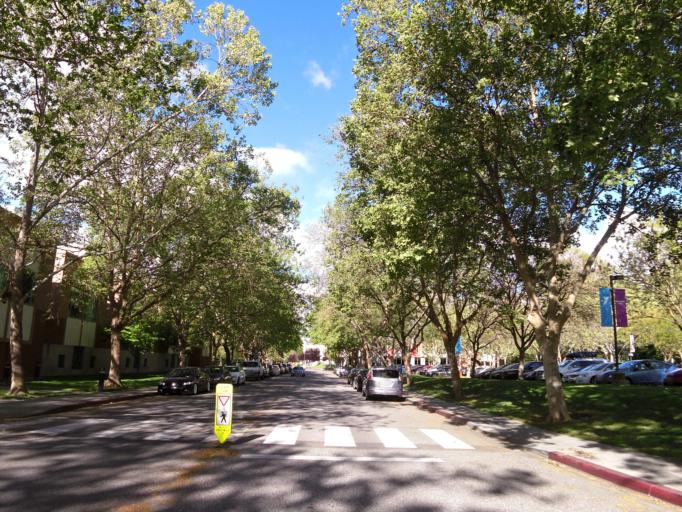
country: US
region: California
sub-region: Santa Clara County
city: Mountain View
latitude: 37.3704
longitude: -122.0804
